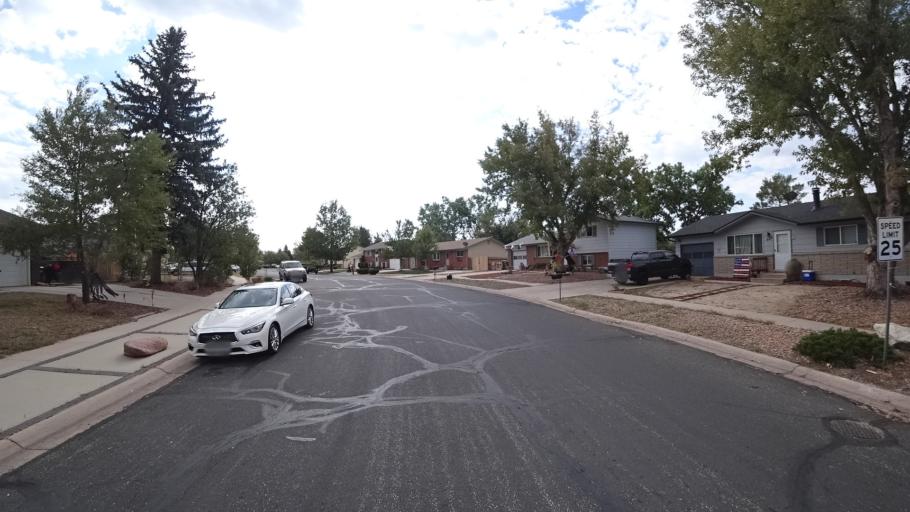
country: US
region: Colorado
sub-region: El Paso County
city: Cimarron Hills
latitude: 38.8464
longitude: -104.7525
